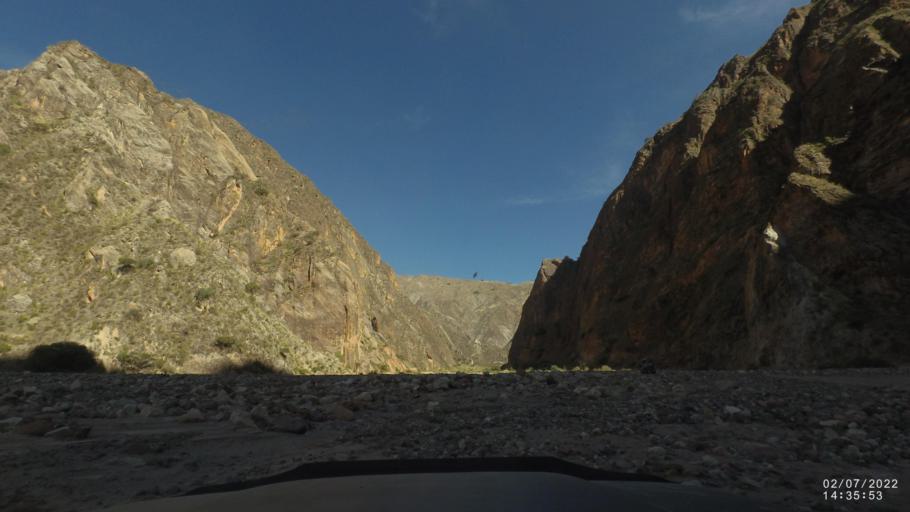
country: BO
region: Cochabamba
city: Irpa Irpa
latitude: -17.8402
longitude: -66.4178
